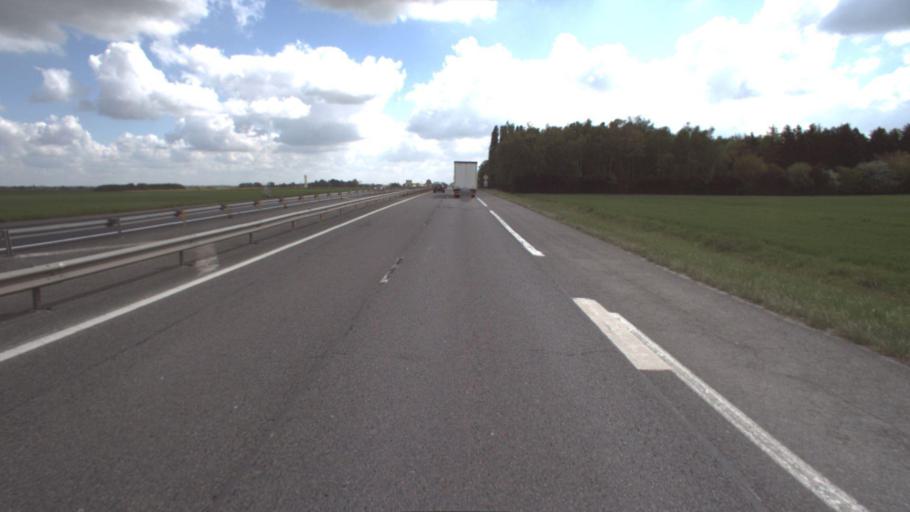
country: FR
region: Ile-de-France
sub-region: Departement de Seine-et-Marne
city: Rozay-en-Brie
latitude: 48.6866
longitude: 2.9746
